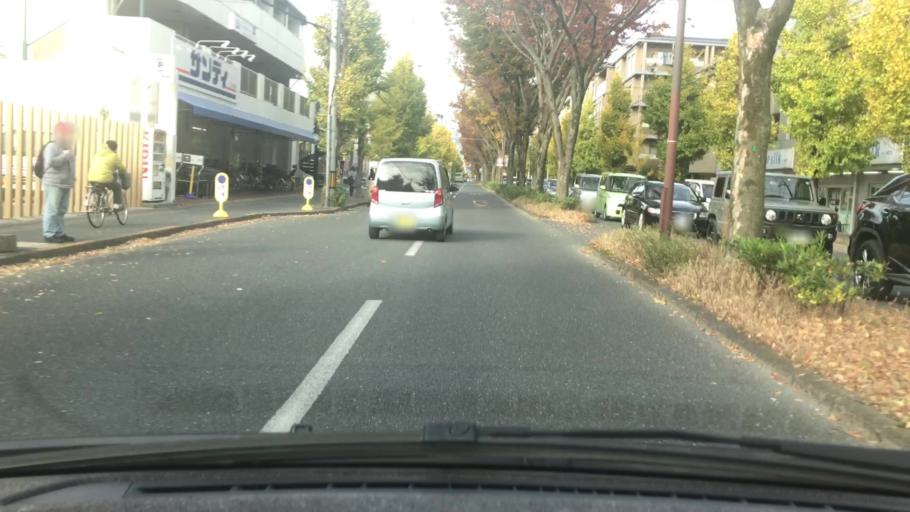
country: JP
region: Kyoto
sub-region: Kyoto-shi
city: Kamigyo-ku
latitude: 35.0441
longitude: 135.7919
